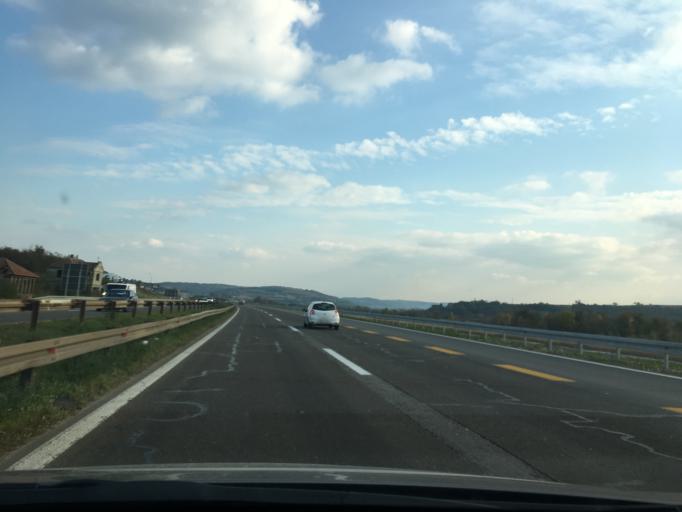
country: RS
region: Central Serbia
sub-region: Belgrade
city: Zvezdara
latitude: 44.7090
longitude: 20.5679
